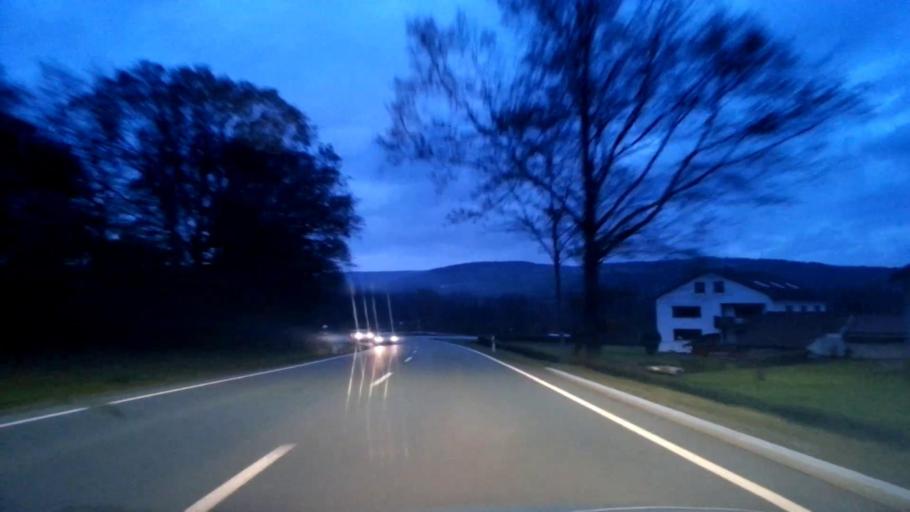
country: DE
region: Bavaria
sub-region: Upper Franconia
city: Kirchenpingarten
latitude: 49.9342
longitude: 11.7428
